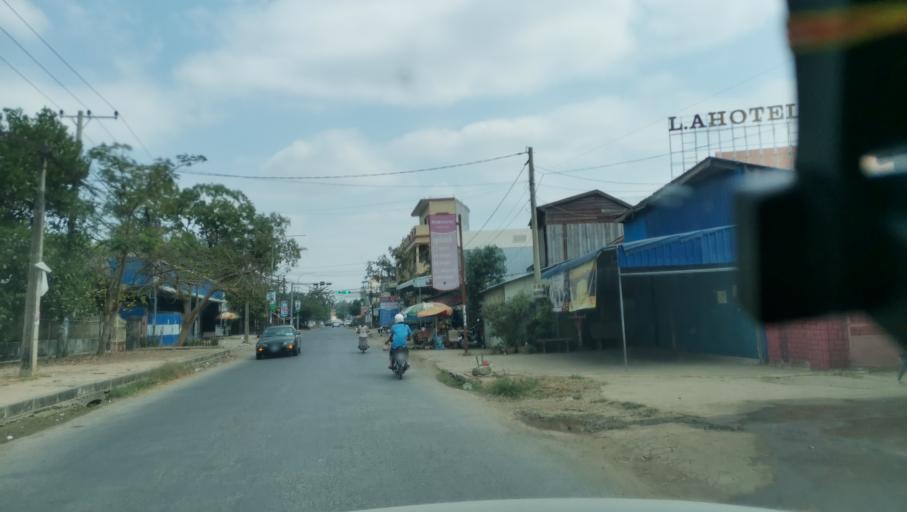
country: KH
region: Battambang
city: Battambang
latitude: 13.0854
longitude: 103.1980
